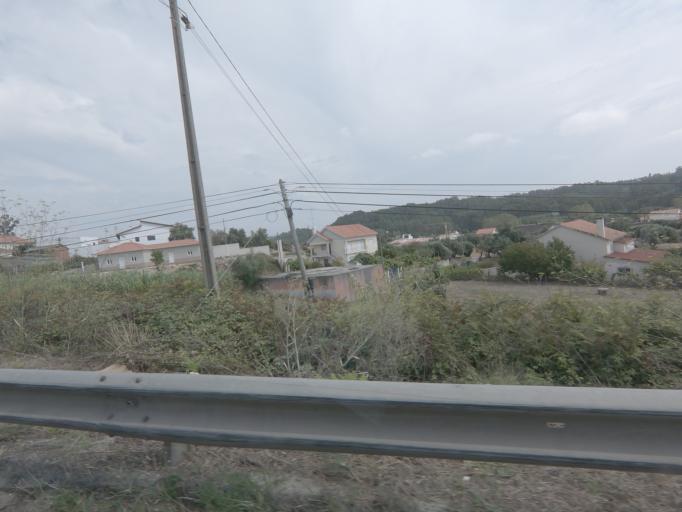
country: PT
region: Leiria
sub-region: Leiria
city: Caranguejeira
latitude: 39.8108
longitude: -8.7397
